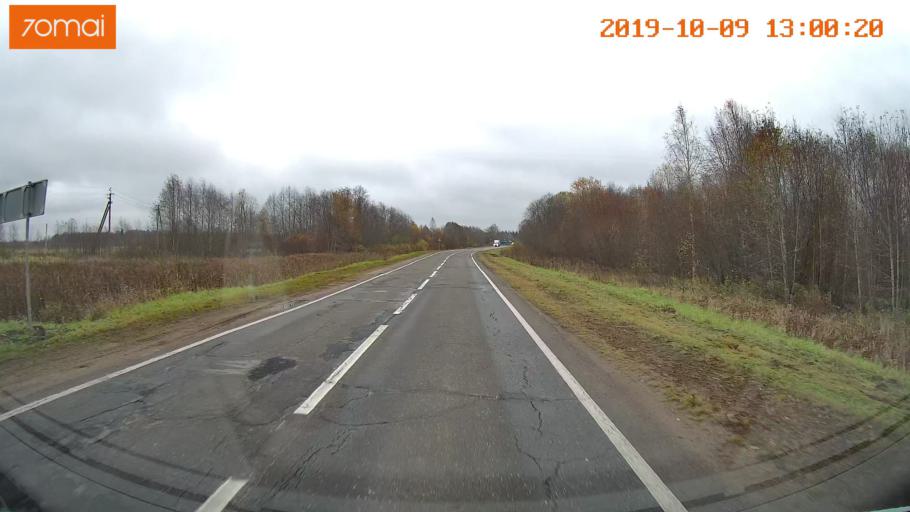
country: RU
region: Jaroslavl
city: Prechistoye
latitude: 58.3780
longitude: 40.4788
